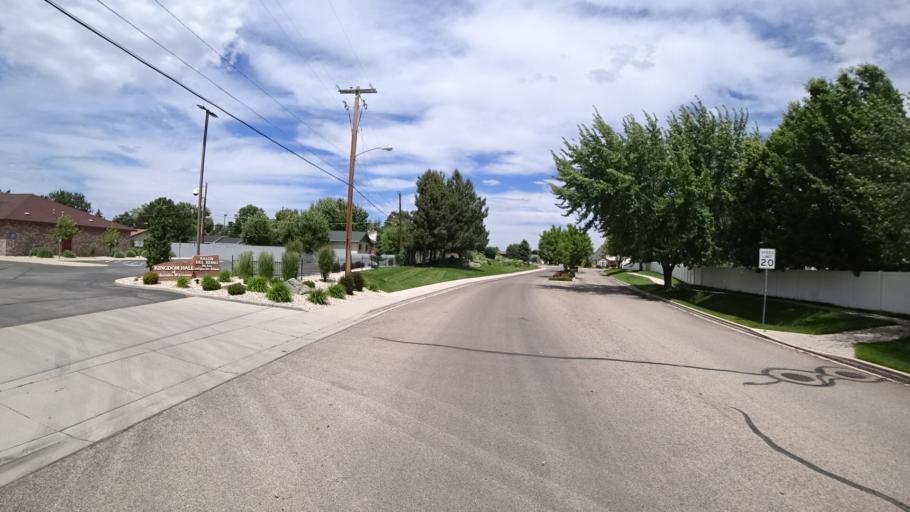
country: US
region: Idaho
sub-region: Ada County
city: Meridian
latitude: 43.6233
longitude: -116.3244
